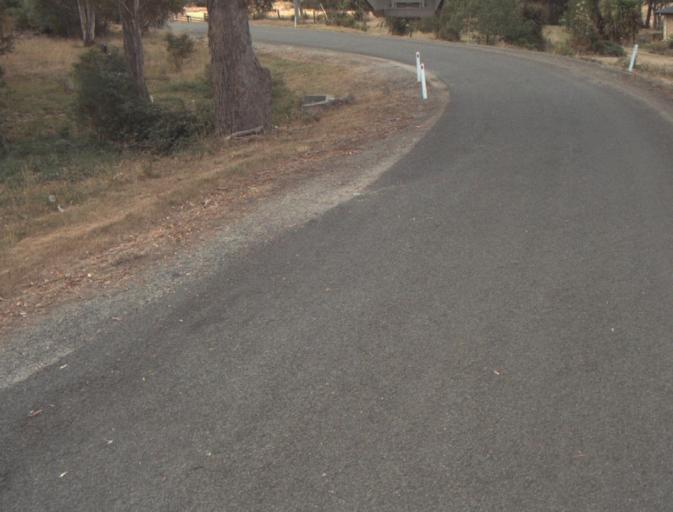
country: AU
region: Tasmania
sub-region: Launceston
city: Mayfield
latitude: -41.3054
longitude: 147.0461
